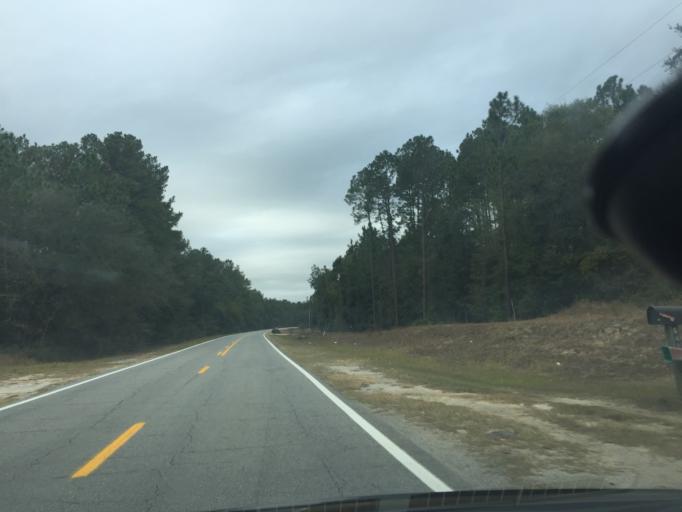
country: US
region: Georgia
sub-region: Chatham County
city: Bloomingdale
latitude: 32.0966
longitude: -81.3788
